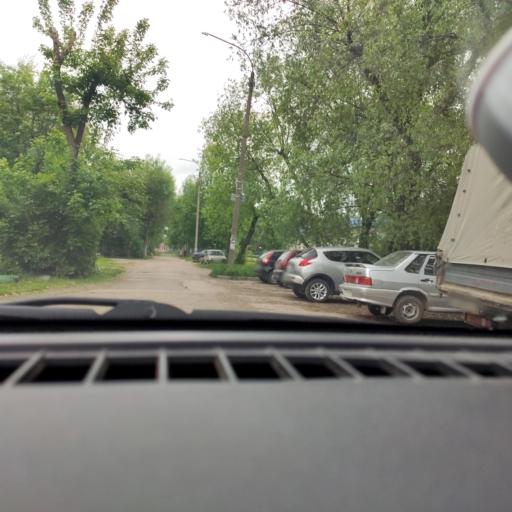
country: RU
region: Perm
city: Ust'-Kachka
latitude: 58.0048
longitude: 55.6680
